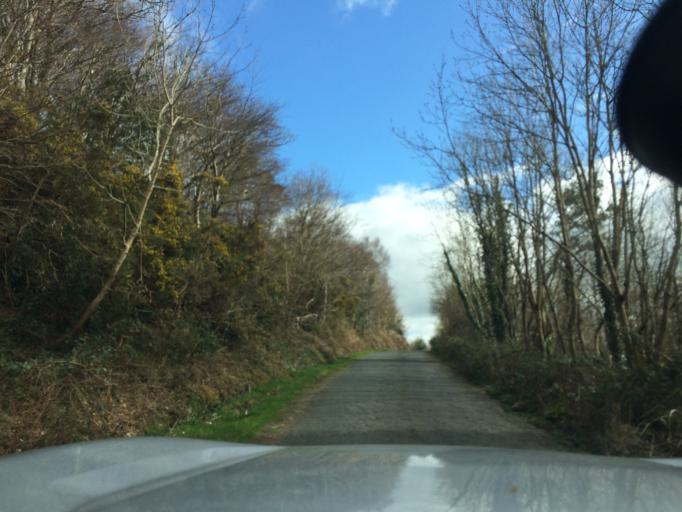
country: IE
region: Munster
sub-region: Waterford
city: Portlaw
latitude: 52.2795
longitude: -7.3701
